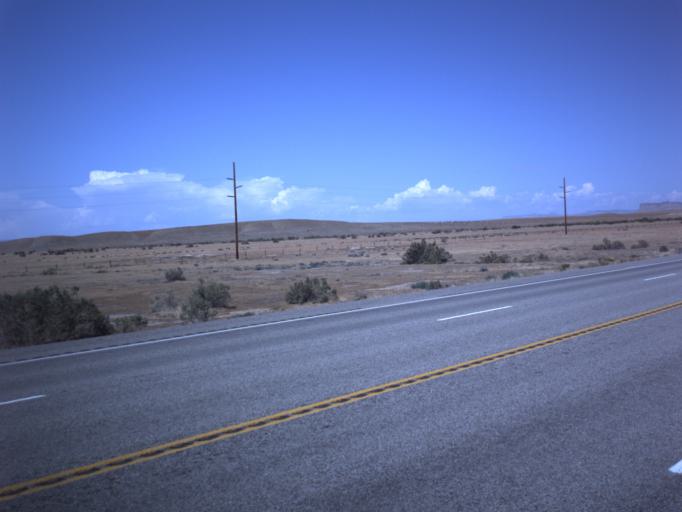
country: US
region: Utah
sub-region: Grand County
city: Moab
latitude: 38.8460
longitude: -109.7974
